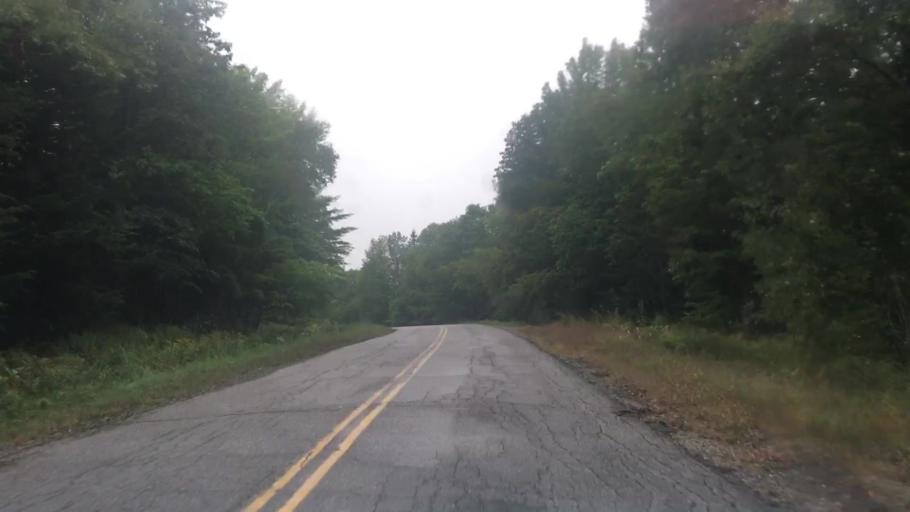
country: US
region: Maine
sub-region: Waldo County
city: Stockton Springs
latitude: 44.5412
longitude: -68.9100
